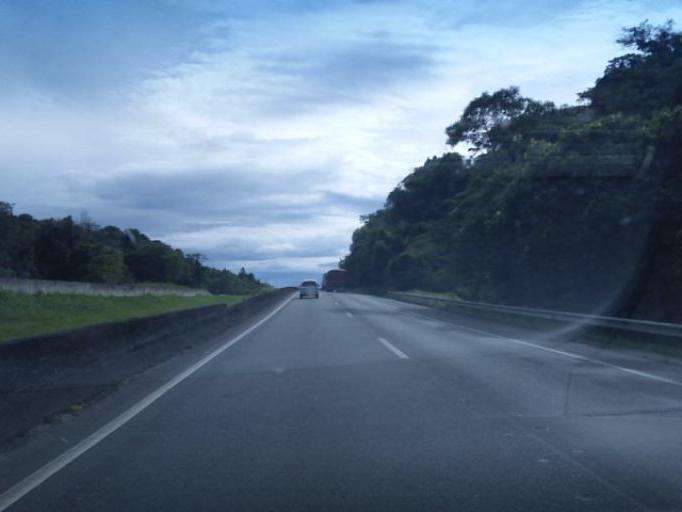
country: BR
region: Sao Paulo
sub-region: Cajati
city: Cajati
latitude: -24.9620
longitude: -48.3398
